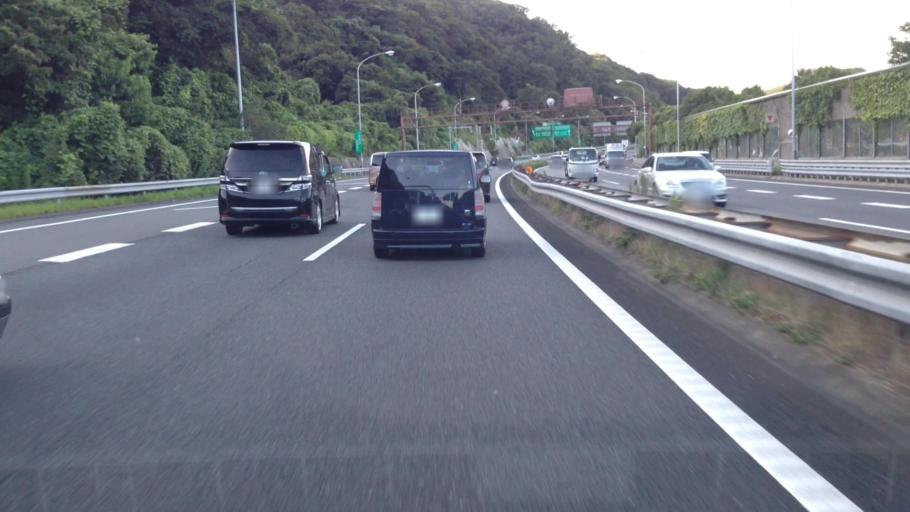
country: JP
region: Kanagawa
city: Zushi
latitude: 35.3395
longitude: 139.5905
